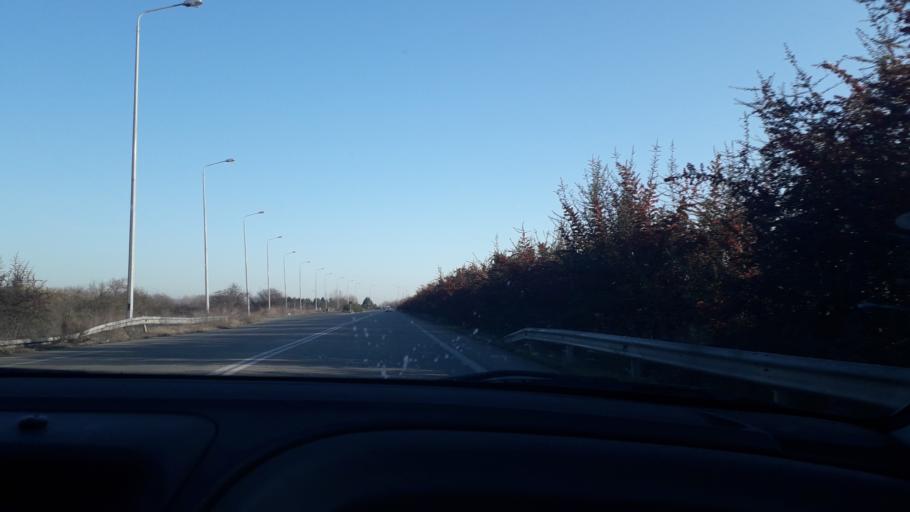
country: GR
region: Central Macedonia
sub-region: Nomos Pellis
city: Palaifyto
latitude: 40.7867
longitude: 22.2890
